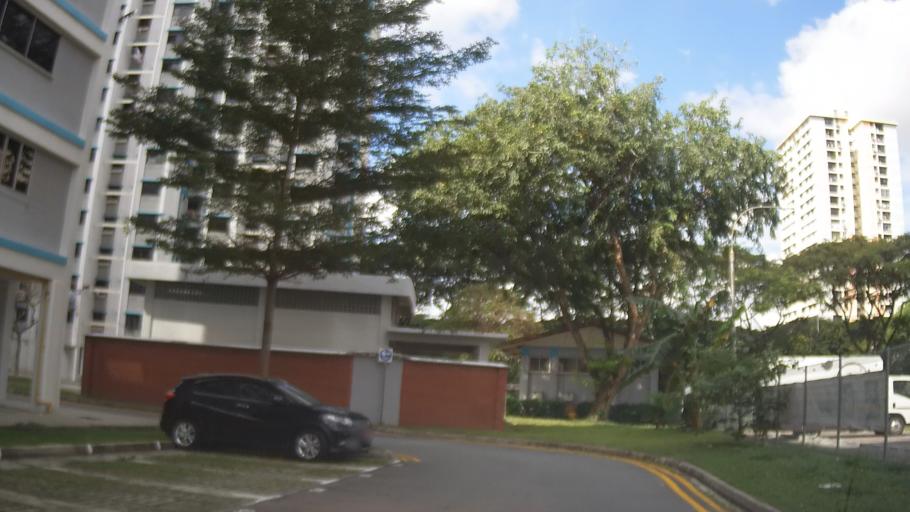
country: SG
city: Singapore
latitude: 1.3176
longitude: 103.8761
